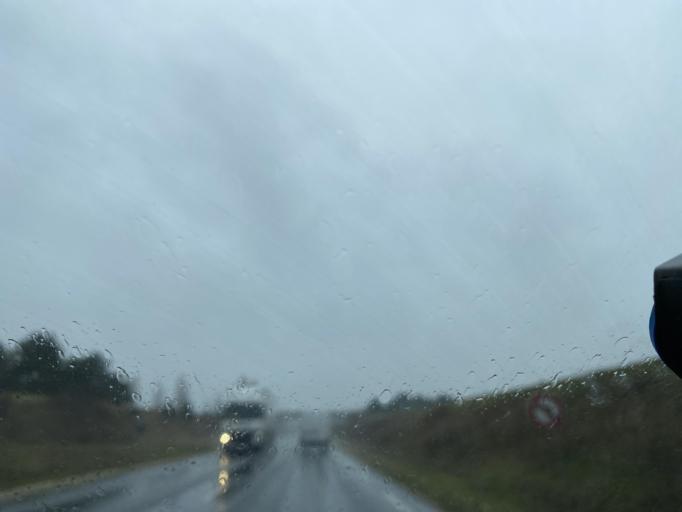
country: FR
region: Centre
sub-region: Departement d'Eure-et-Loir
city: Mainvilliers
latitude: 48.4584
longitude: 1.4522
